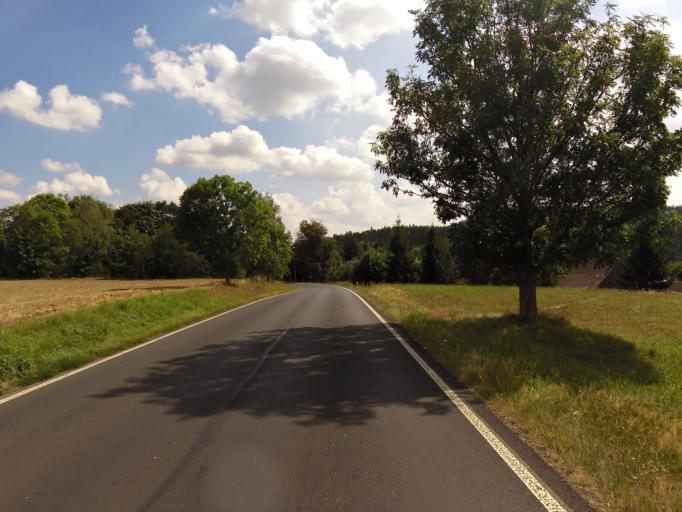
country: CZ
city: Osecna
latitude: 50.7010
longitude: 14.8951
